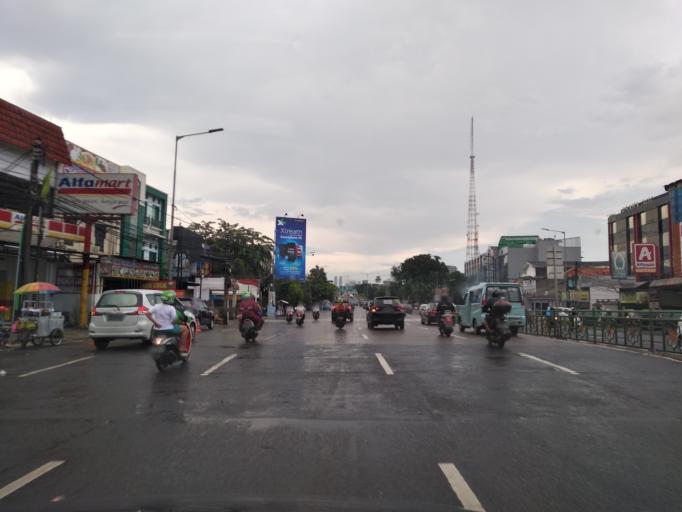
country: ID
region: Jakarta Raya
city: Jakarta
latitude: -6.2252
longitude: 106.8628
